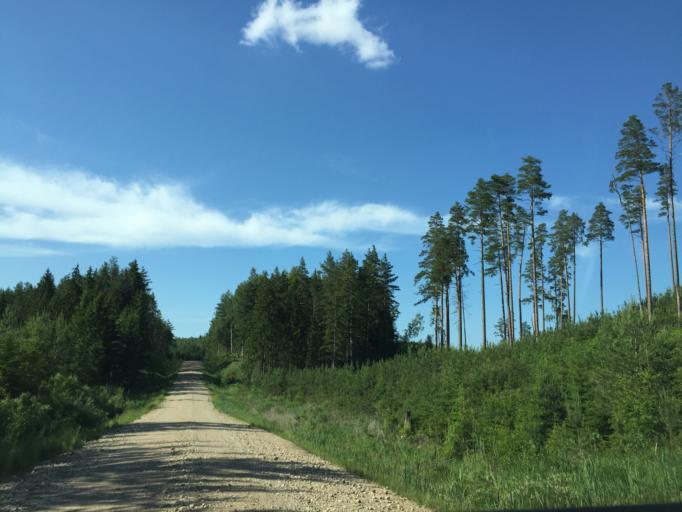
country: LV
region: Tukuma Rajons
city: Tukums
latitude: 57.0202
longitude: 23.2253
